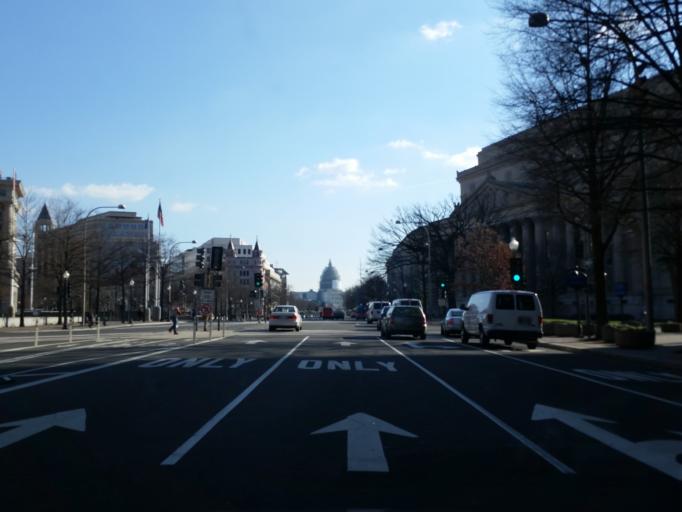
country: US
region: Washington, D.C.
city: Washington, D.C.
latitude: 38.8940
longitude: -77.0246
